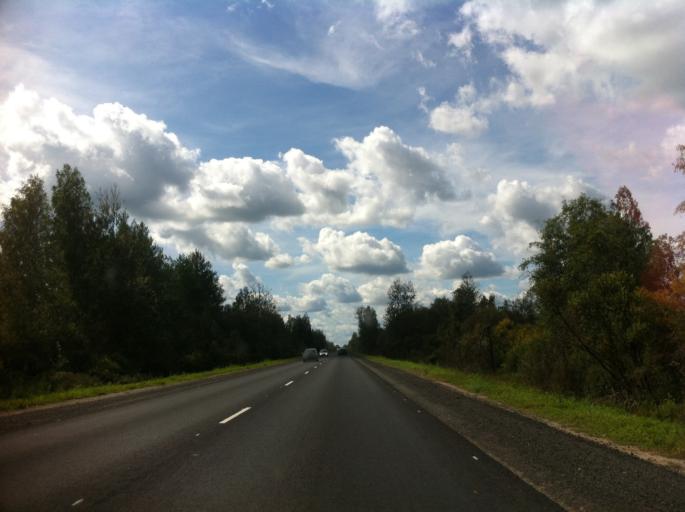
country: RU
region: Pskov
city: Izborsk
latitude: 57.7487
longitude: 28.0423
